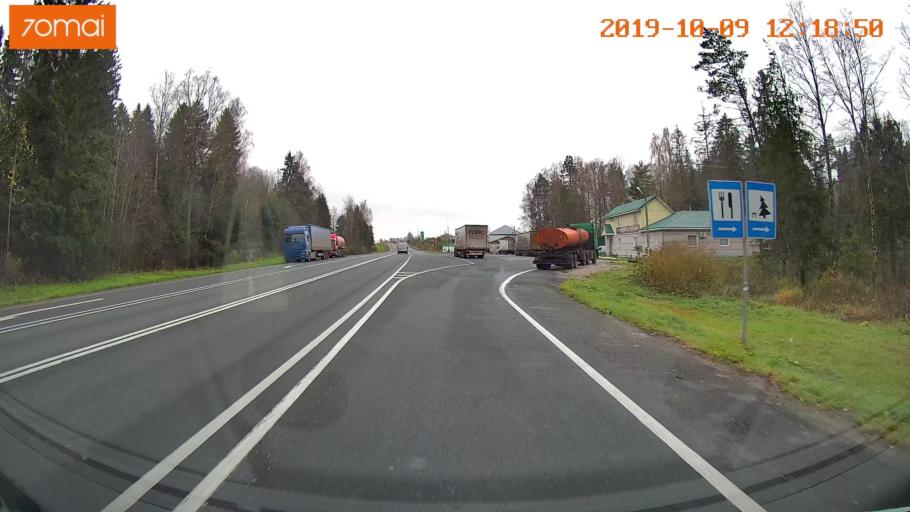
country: RU
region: Jaroslavl
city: Prechistoye
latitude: 58.4371
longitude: 40.3214
